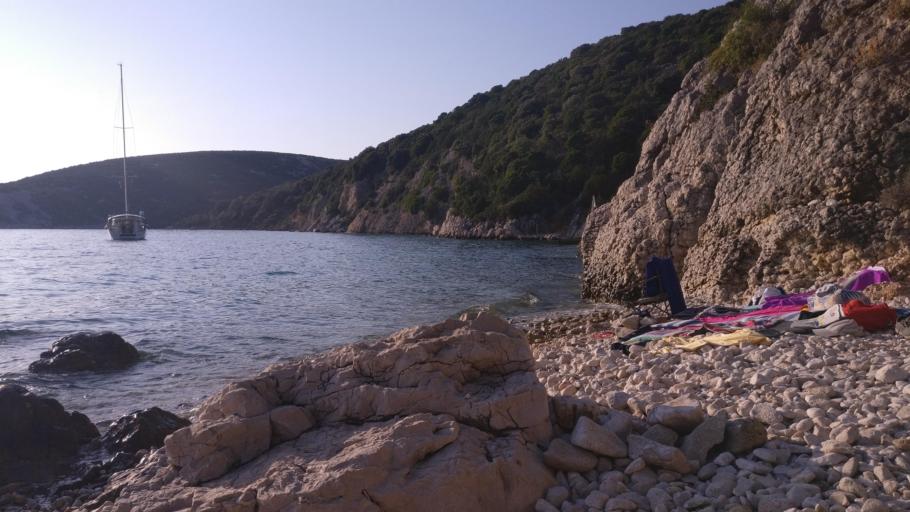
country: HR
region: Primorsko-Goranska
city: Lopar
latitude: 44.8198
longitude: 14.7107
